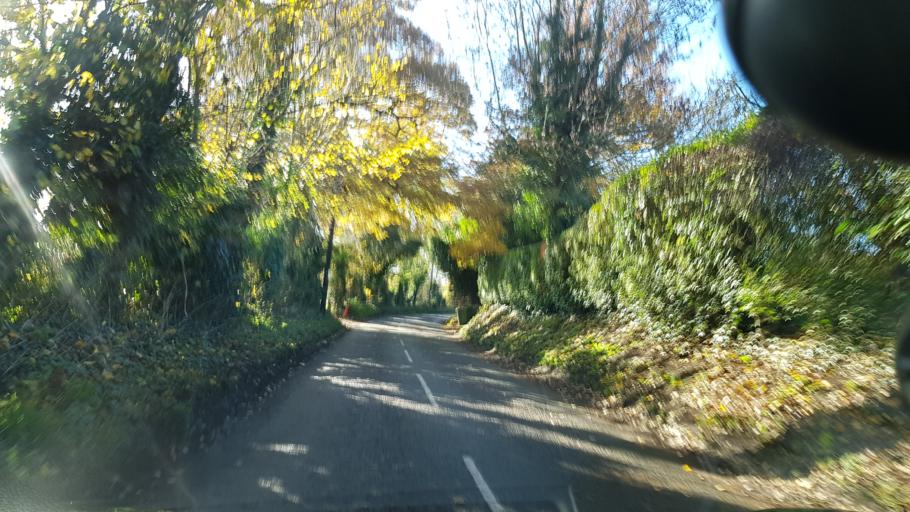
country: GB
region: England
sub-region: Surrey
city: Normandy
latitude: 51.2207
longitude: -0.6686
